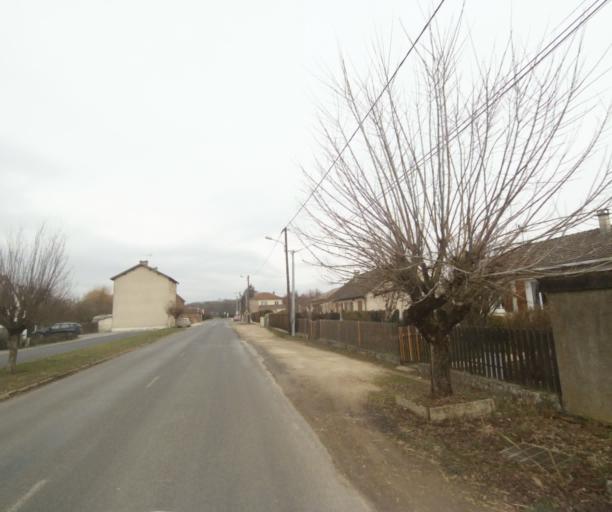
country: FR
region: Champagne-Ardenne
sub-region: Departement de la Haute-Marne
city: Villiers-en-Lieu
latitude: 48.6823
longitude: 4.8836
